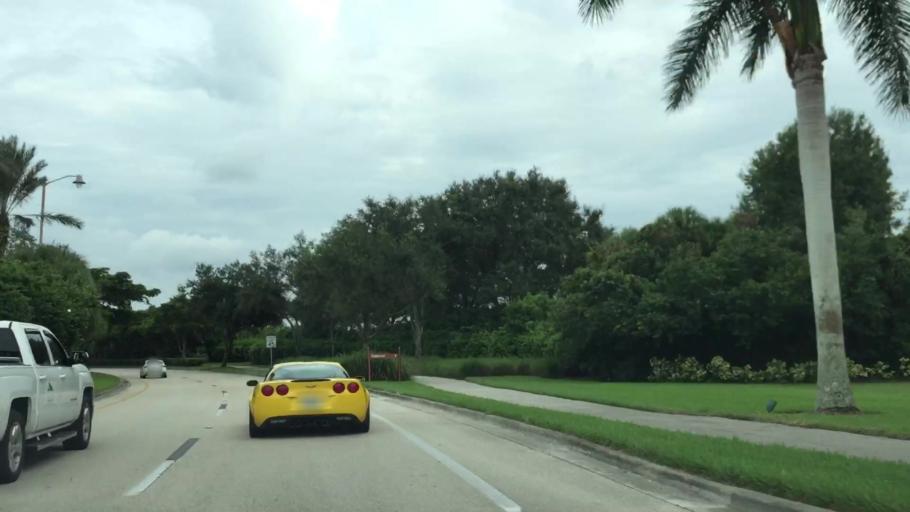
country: US
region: Florida
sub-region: Lee County
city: Estero
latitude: 26.3955
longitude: -81.7947
